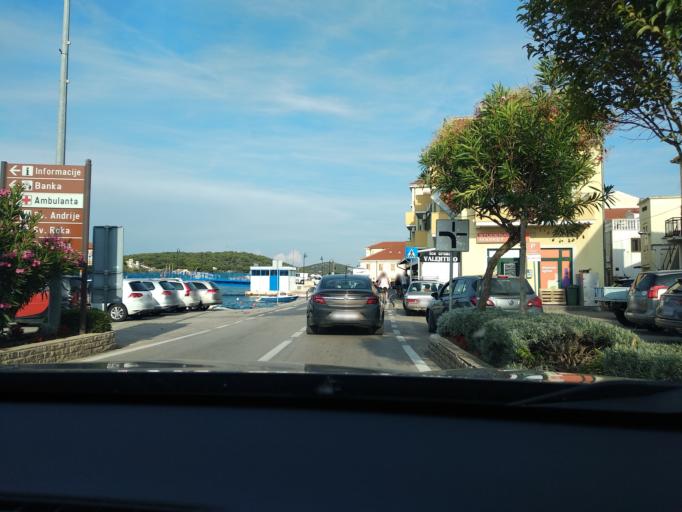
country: HR
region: Sibensko-Kniniska
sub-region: Grad Sibenik
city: Tisno
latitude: 43.8011
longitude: 15.6487
